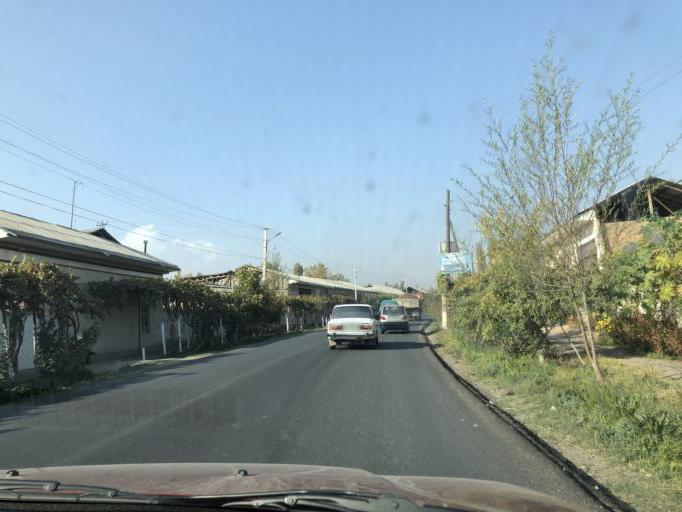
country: UZ
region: Namangan
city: Chust Shahri
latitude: 41.0677
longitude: 71.2048
